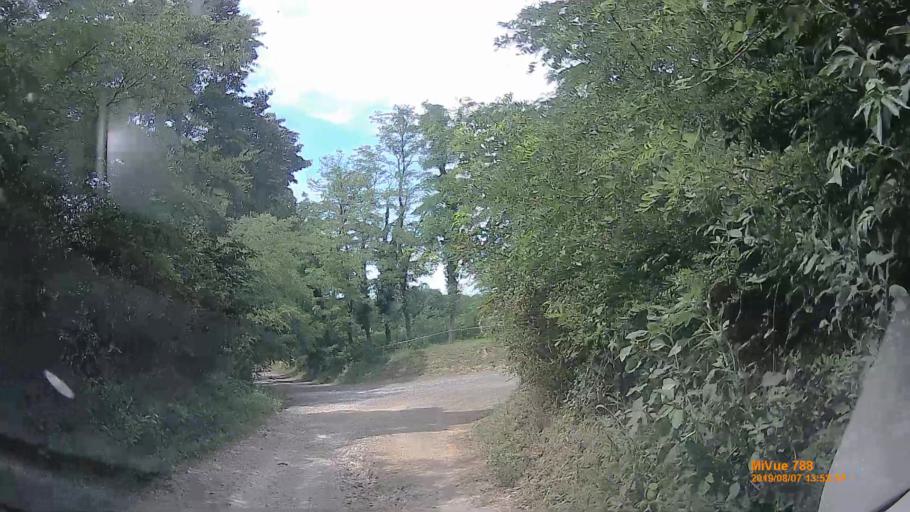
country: HU
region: Zala
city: Cserszegtomaj
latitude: 46.8936
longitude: 17.1784
